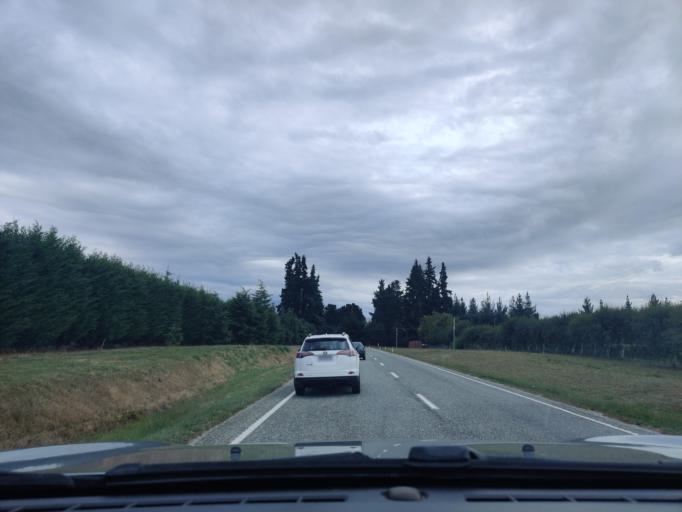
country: NZ
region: Otago
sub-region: Queenstown-Lakes District
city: Wanaka
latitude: -44.7027
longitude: 169.1948
